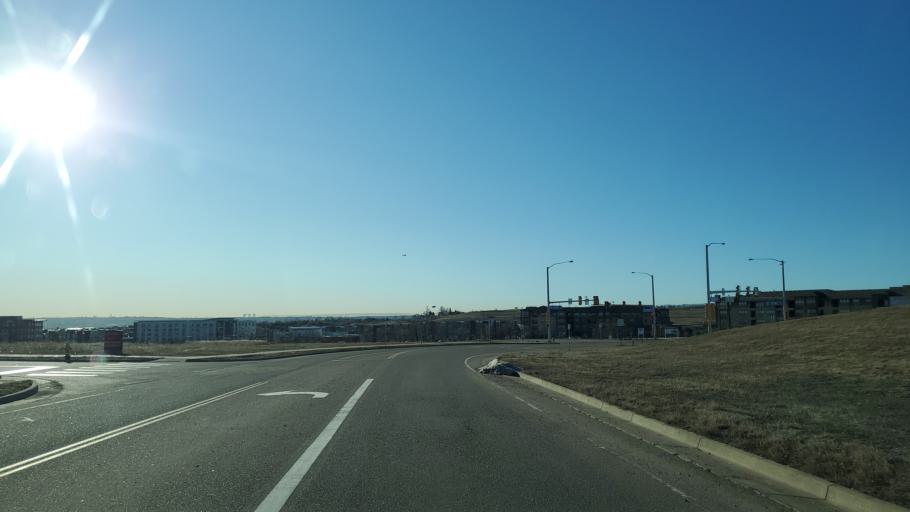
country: US
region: Colorado
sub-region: Broomfield County
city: Broomfield
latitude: 39.9098
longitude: -105.0932
